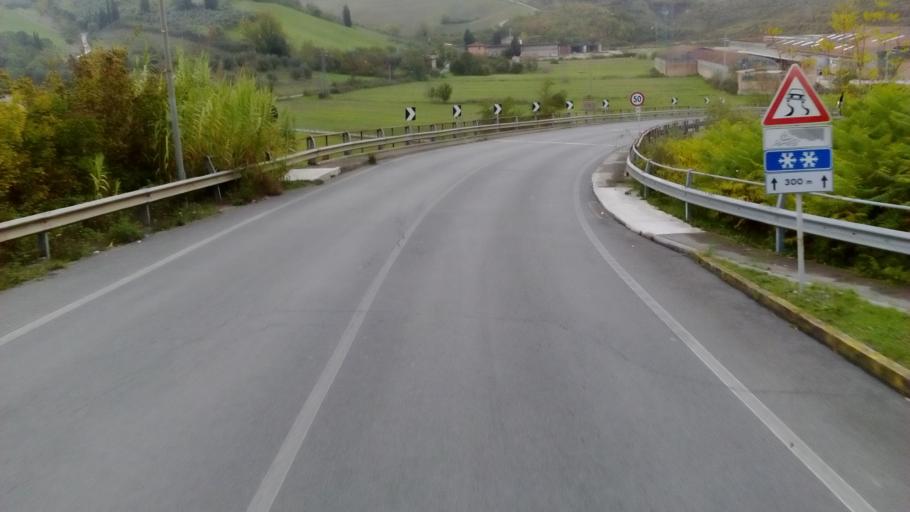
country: IT
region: Tuscany
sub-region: Province of Florence
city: Castelfiorentino
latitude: 43.6066
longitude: 10.9752
